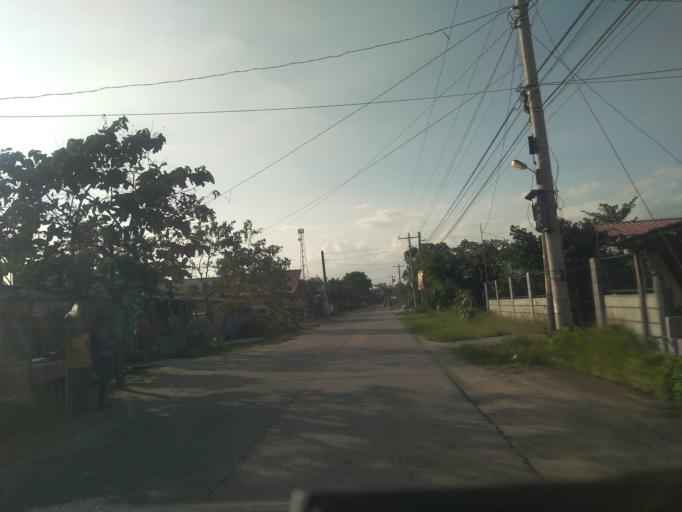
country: PH
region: Central Luzon
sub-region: Province of Pampanga
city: Bulaon
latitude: 15.0883
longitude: 120.6917
